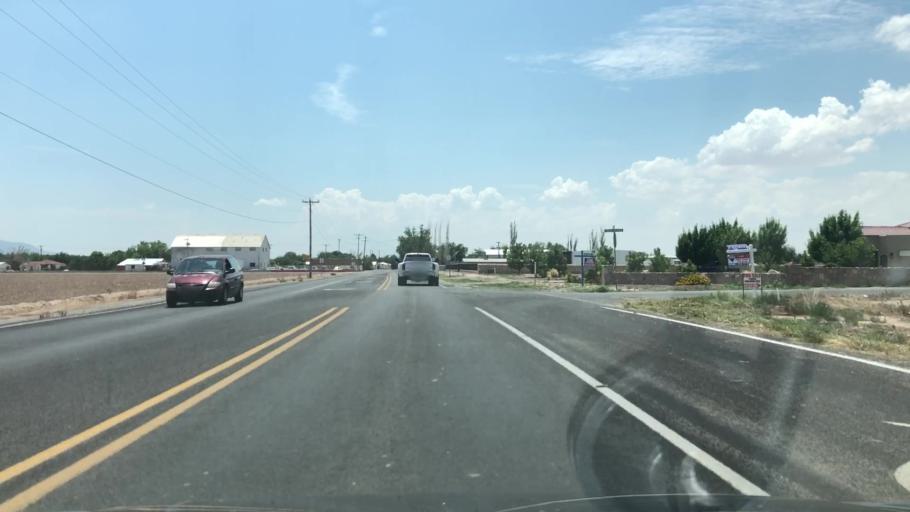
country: US
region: New Mexico
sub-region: Dona Ana County
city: La Union
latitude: 31.9588
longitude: -106.6466
